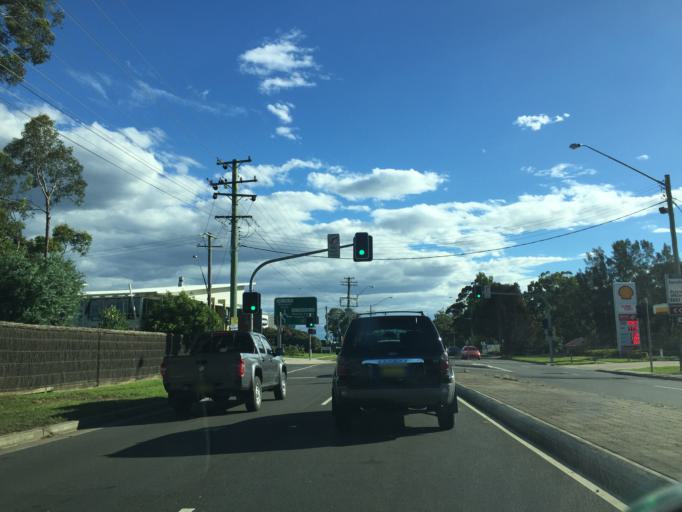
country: AU
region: New South Wales
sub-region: The Hills Shire
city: Glenhaven
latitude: -33.6938
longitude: 151.0320
